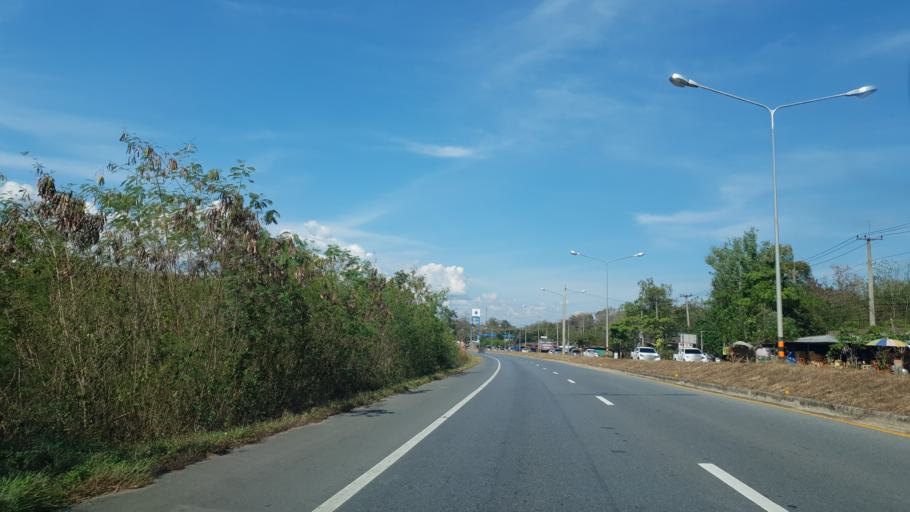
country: TH
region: Phrae
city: Den Chai
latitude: 17.9521
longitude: 100.0683
